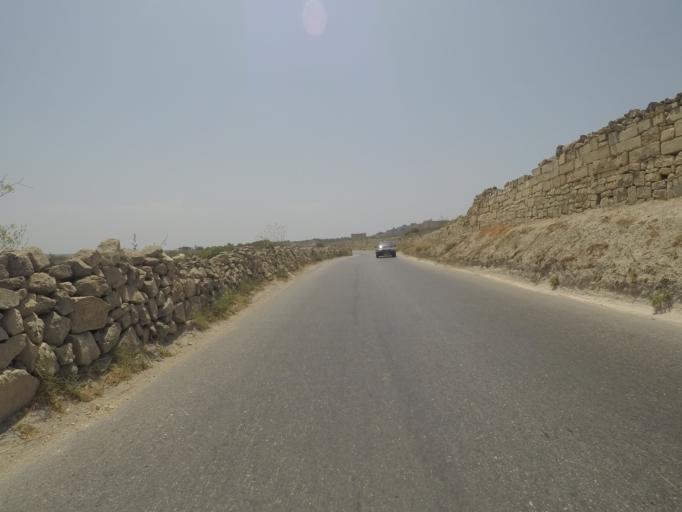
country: MT
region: Is-Siggiewi
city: Siggiewi
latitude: 35.8658
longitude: 14.4173
